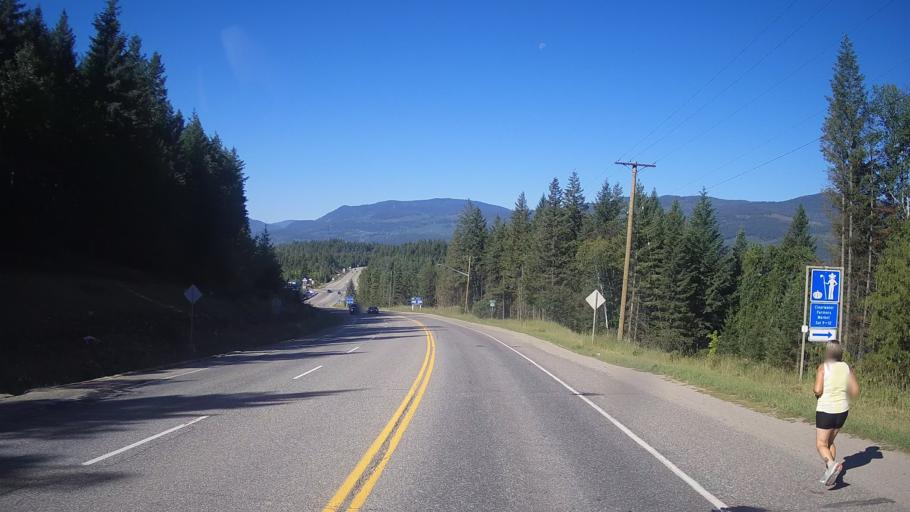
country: CA
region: British Columbia
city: Chase
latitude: 51.6500
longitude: -120.0450
